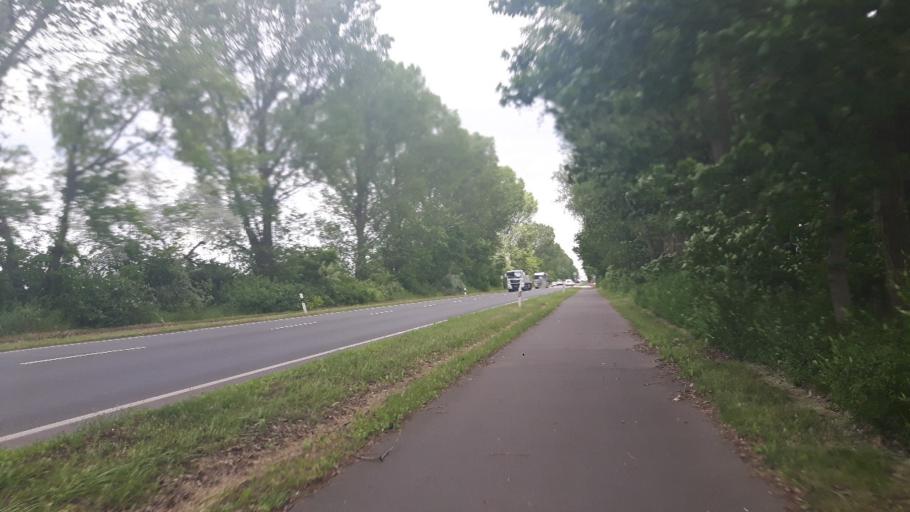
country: DE
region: Berlin
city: Stadtrandsiedlung Malchow
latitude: 52.5906
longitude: 13.4905
